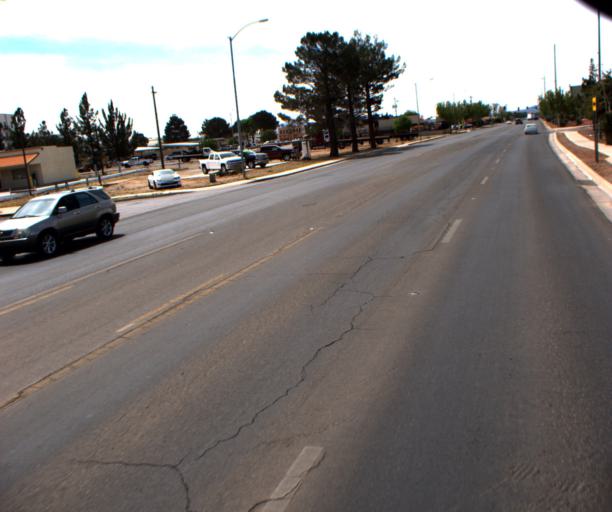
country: US
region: Arizona
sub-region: Cochise County
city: Douglas
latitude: 31.3468
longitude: -109.5563
